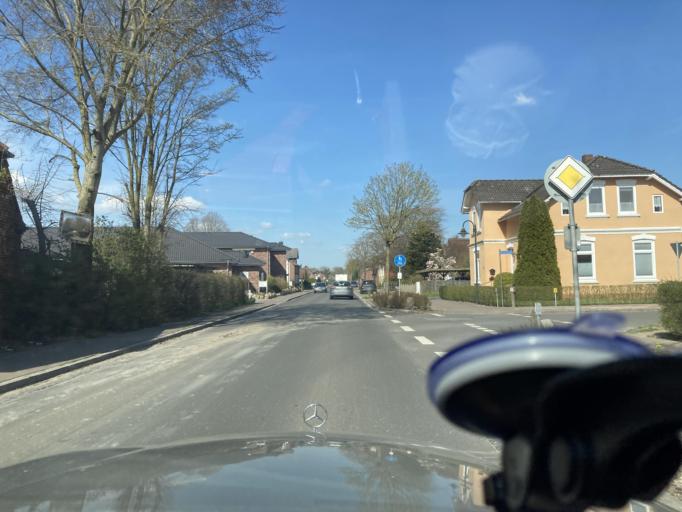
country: DE
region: Schleswig-Holstein
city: Lehe
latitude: 54.3369
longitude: 9.0227
